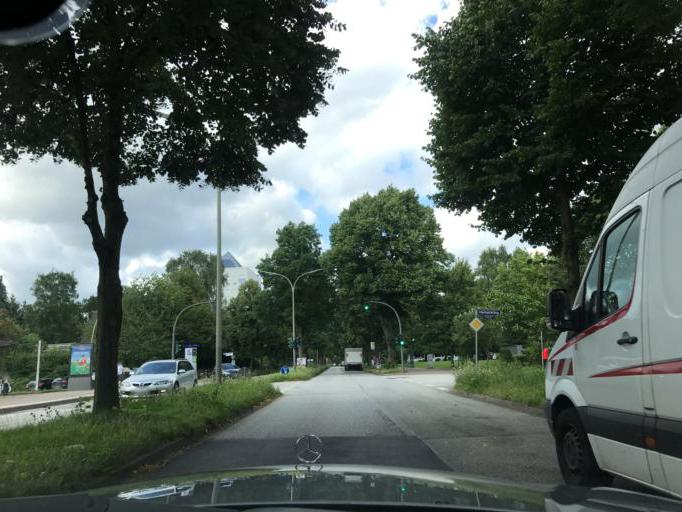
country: DE
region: Hamburg
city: Bergedorf
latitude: 53.5069
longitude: 10.2111
